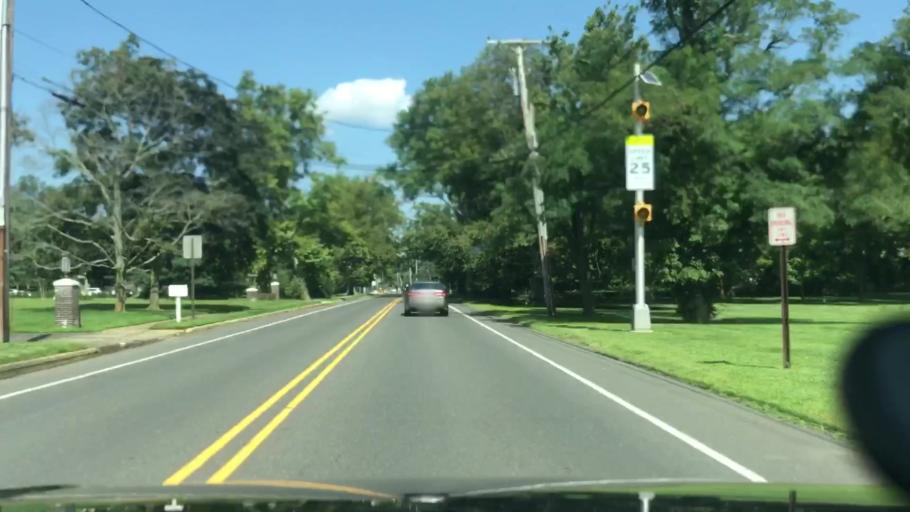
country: US
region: New Jersey
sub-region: Monmouth County
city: Little Silver
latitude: 40.3346
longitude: -74.0282
